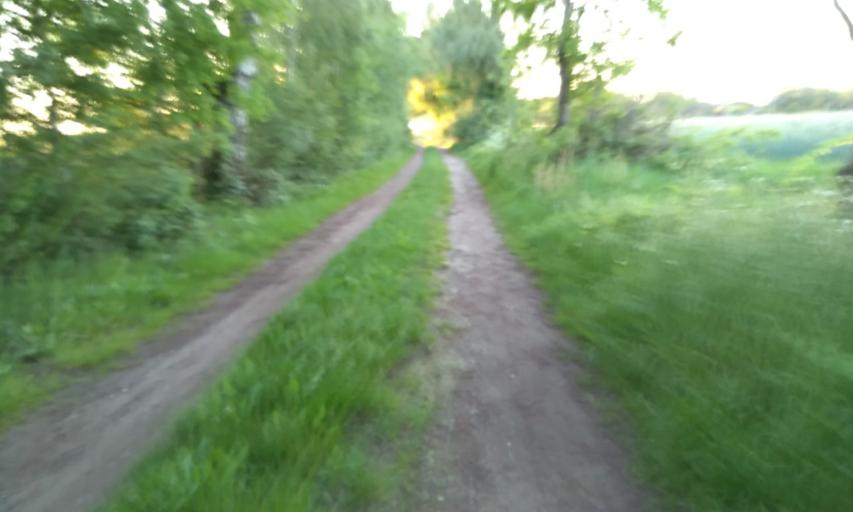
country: DE
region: Lower Saxony
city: Bargstedt
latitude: 53.4365
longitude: 9.4287
